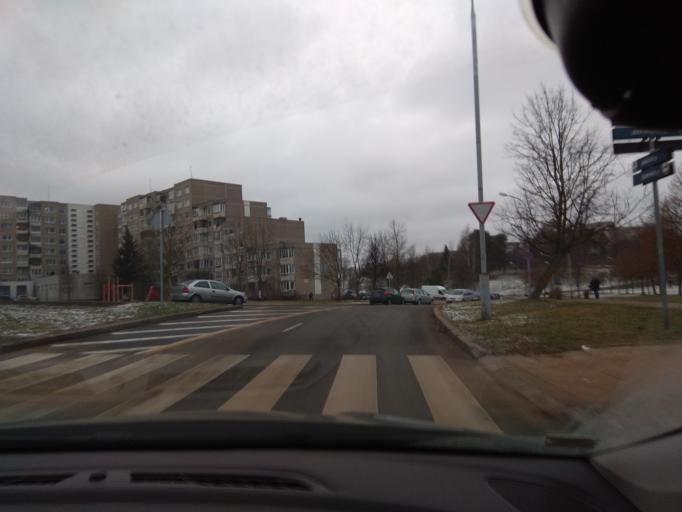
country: LT
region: Vilnius County
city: Pasilaiciai
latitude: 54.7282
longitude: 25.2266
